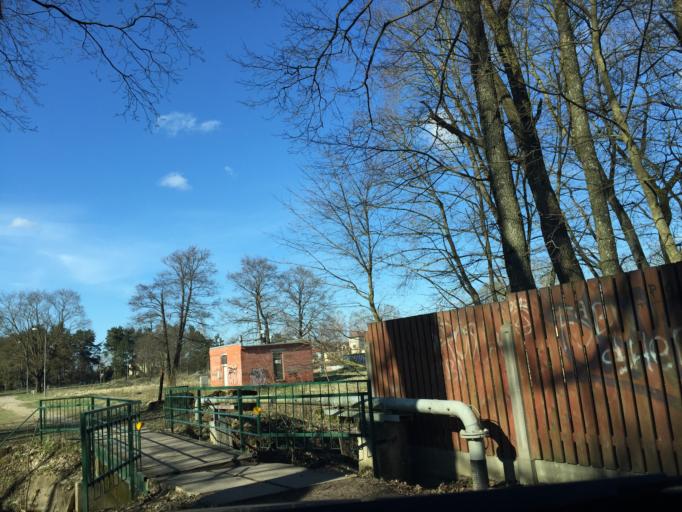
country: LV
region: Kekava
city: Kekava
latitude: 56.8523
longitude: 24.2000
